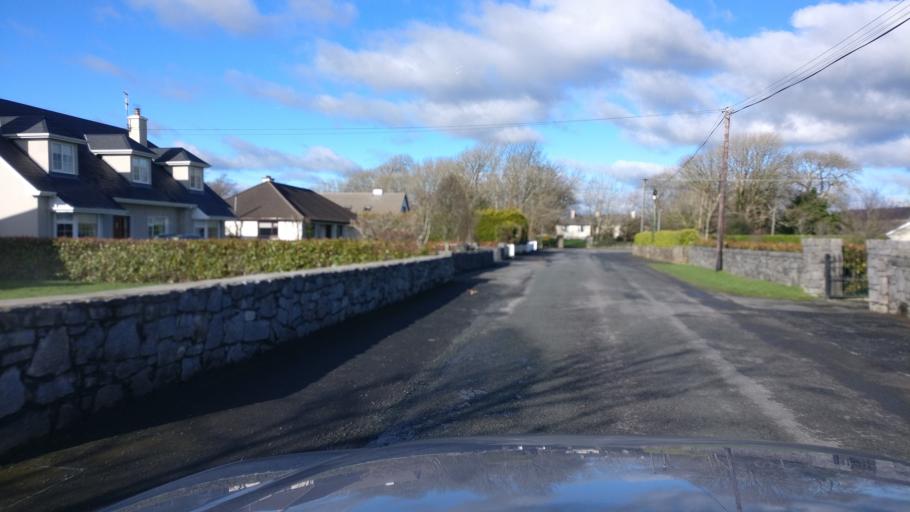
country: IE
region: Connaught
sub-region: County Galway
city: Oranmore
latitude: 53.2781
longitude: -8.9065
